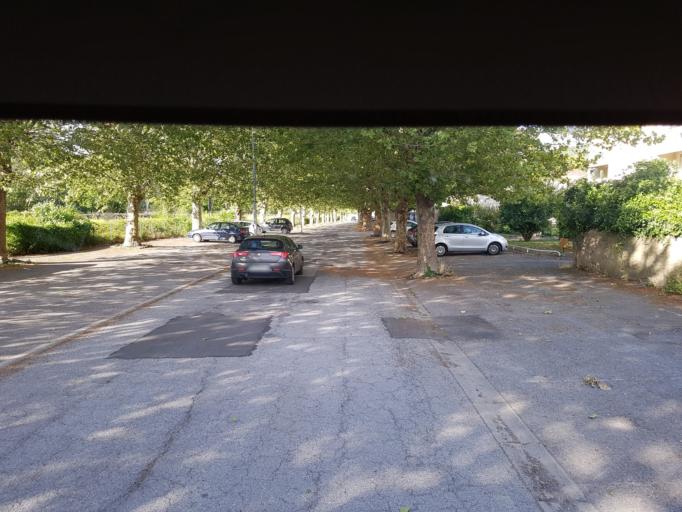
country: FR
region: Lorraine
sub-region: Departement de la Moselle
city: Sierck-les-Bains
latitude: 49.4443
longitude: 6.3624
